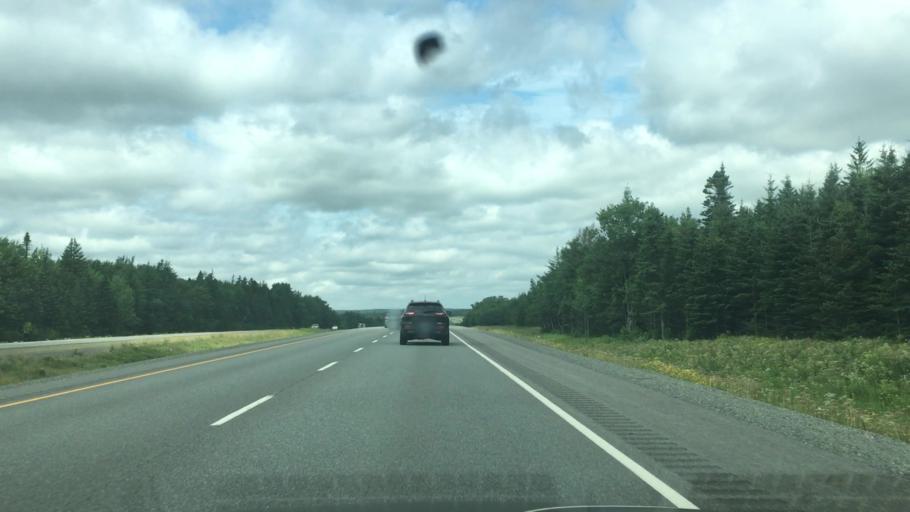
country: CA
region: Nova Scotia
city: Springhill
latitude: 45.7200
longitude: -64.0509
